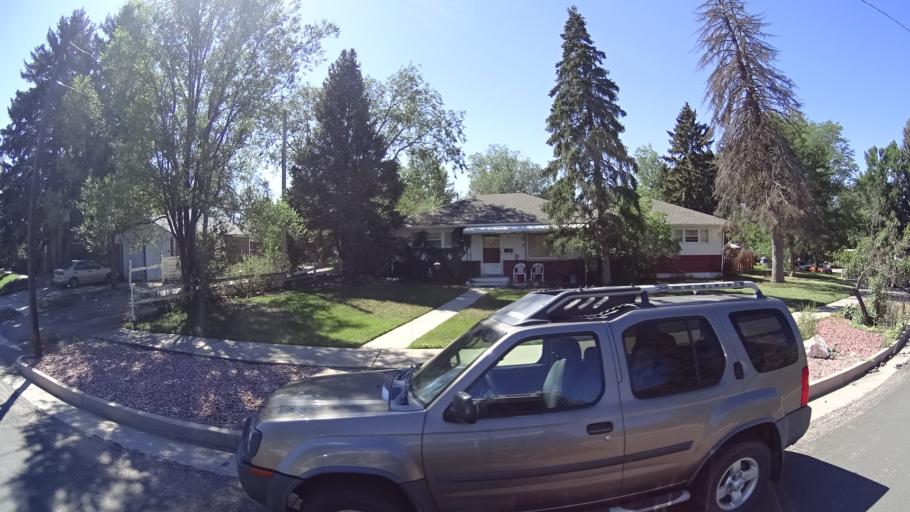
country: US
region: Colorado
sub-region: El Paso County
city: Colorado Springs
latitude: 38.8551
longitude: -104.8056
